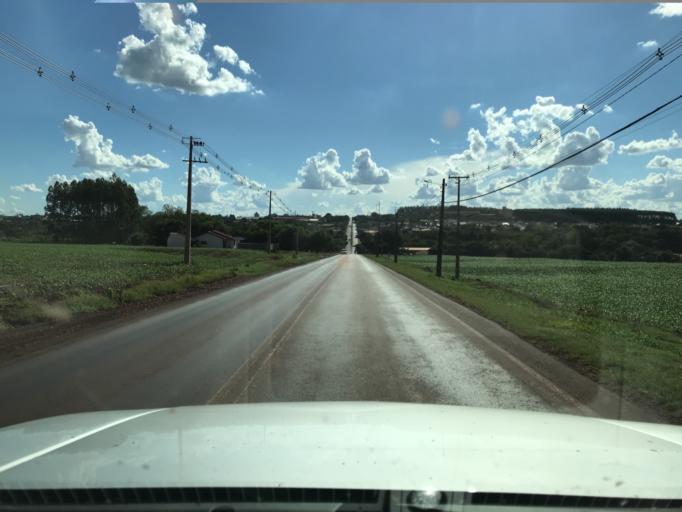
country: BR
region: Parana
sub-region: Palotina
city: Palotina
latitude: -24.2769
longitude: -53.8169
